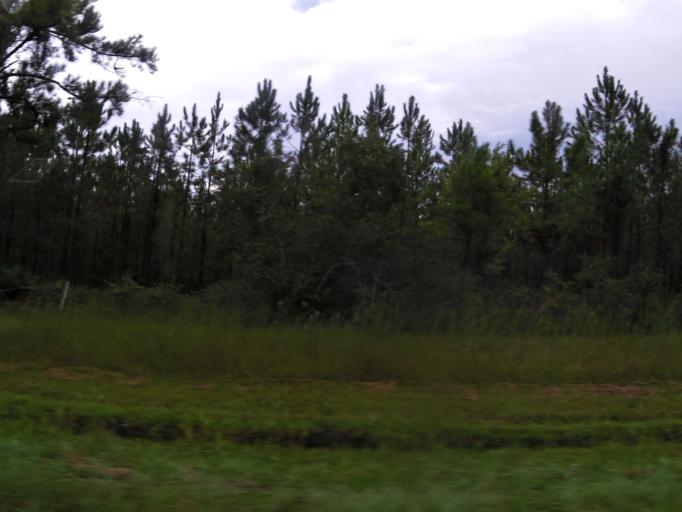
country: US
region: Florida
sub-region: Duval County
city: Baldwin
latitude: 30.4017
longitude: -81.9712
